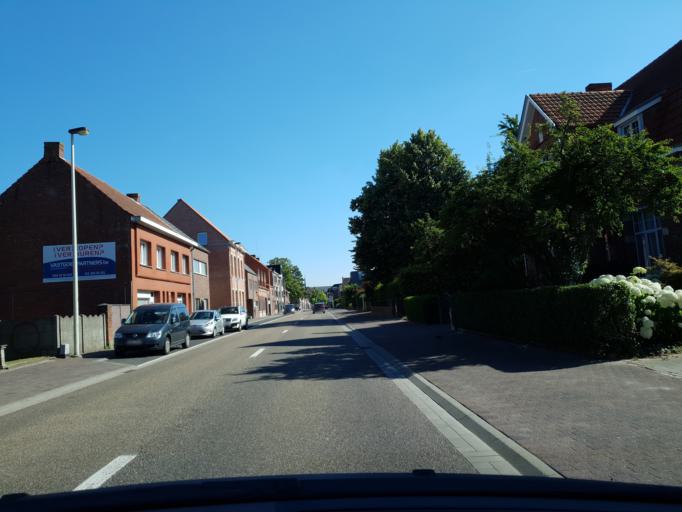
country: BE
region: Flanders
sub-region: Provincie Antwerpen
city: Beerse
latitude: 51.3239
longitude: 4.8561
